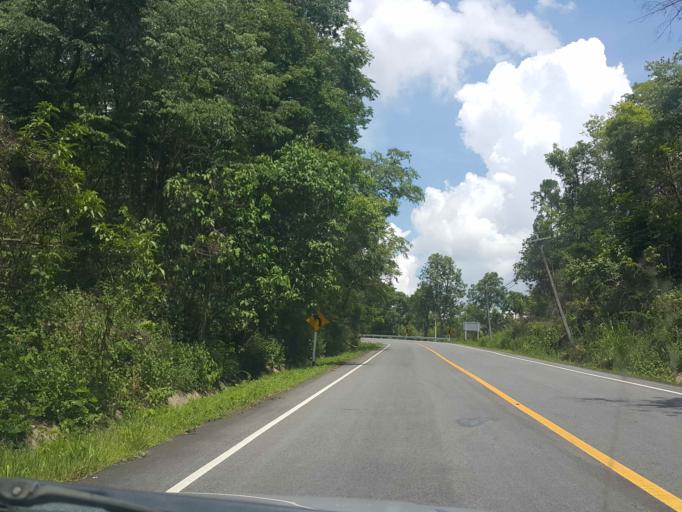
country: TH
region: Phayao
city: Chiang Muan
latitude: 18.8479
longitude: 100.3338
